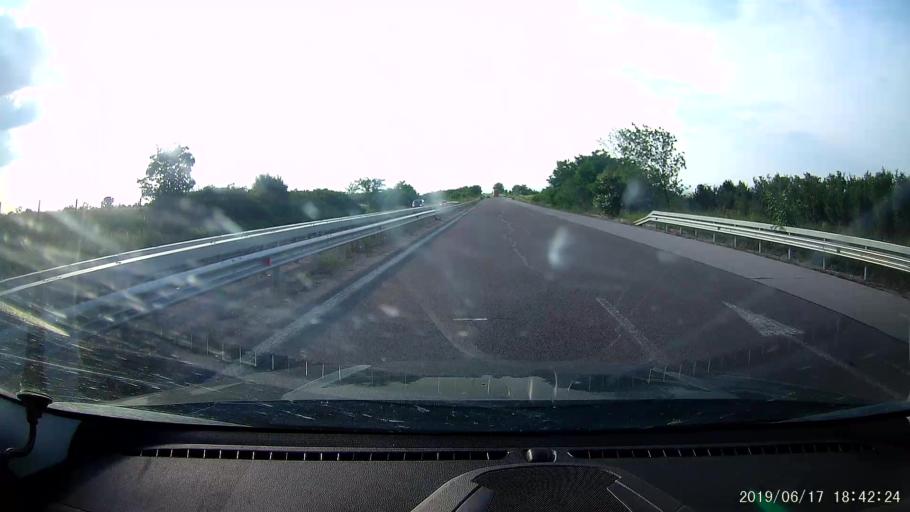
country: BG
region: Stara Zagora
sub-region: Obshtina Chirpan
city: Chirpan
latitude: 42.1906
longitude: 25.2378
